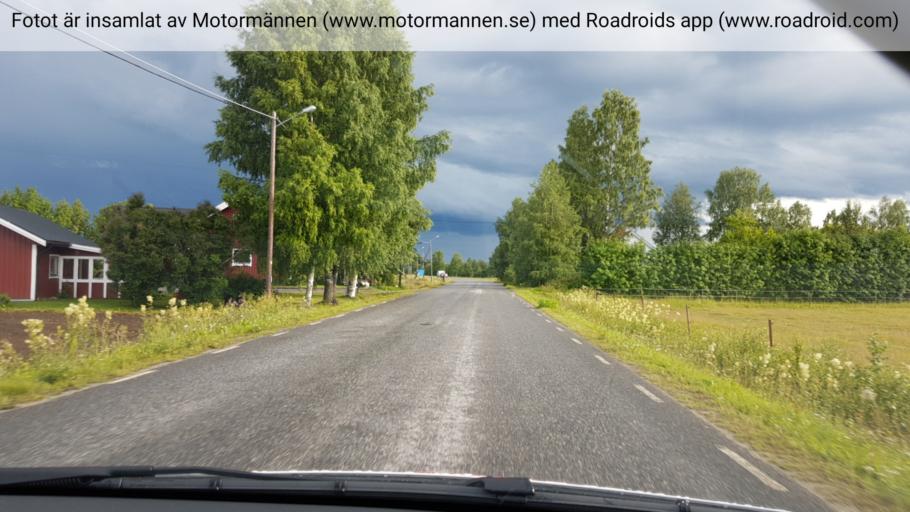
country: SE
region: Vaesterbotten
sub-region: Vannas Kommun
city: Vannasby
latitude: 63.9277
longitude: 19.8551
